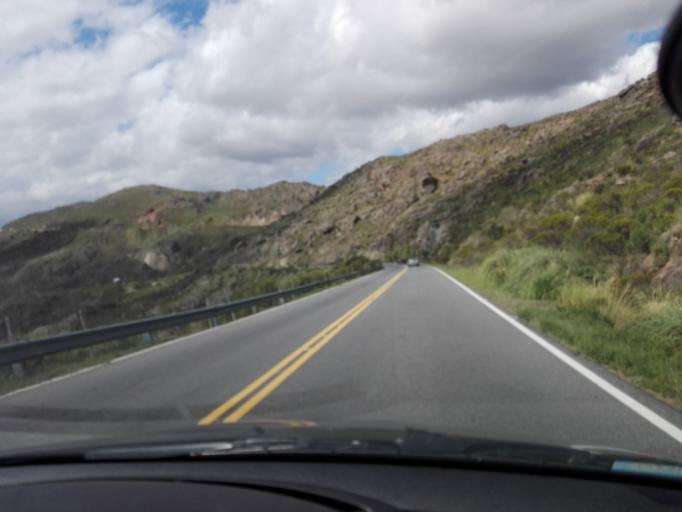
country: AR
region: Cordoba
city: Mina Clavero
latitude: -31.7867
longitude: -64.9119
